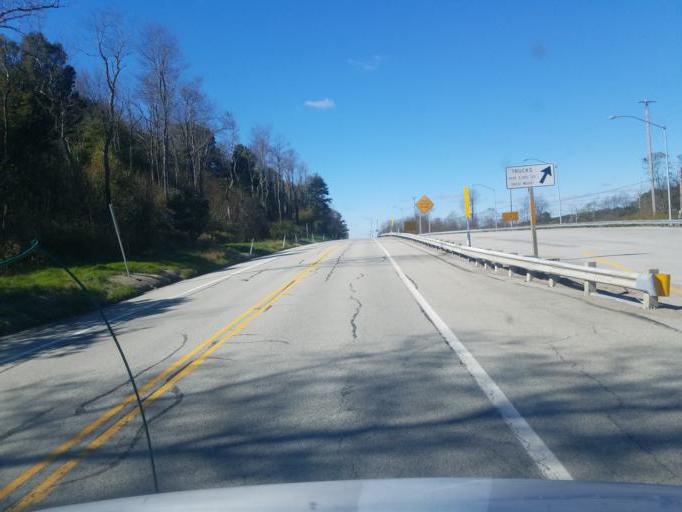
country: US
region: Pennsylvania
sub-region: Westmoreland County
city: Waterford
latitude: 40.1816
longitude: -79.1368
